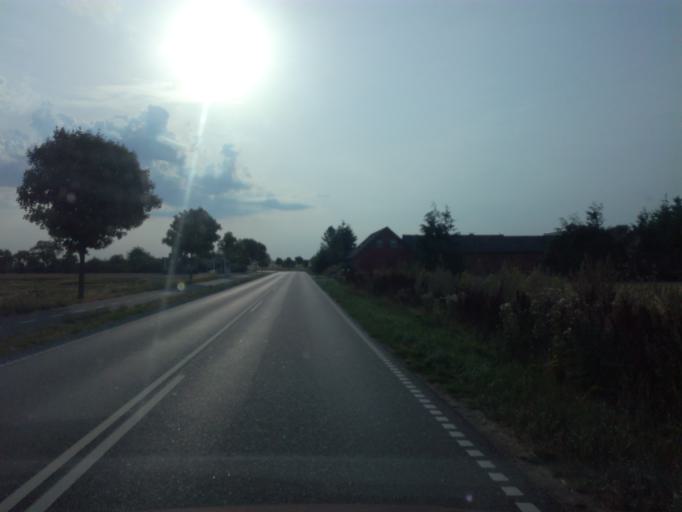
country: DK
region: South Denmark
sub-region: Vejle Kommune
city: Borkop
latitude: 55.6365
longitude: 9.6248
